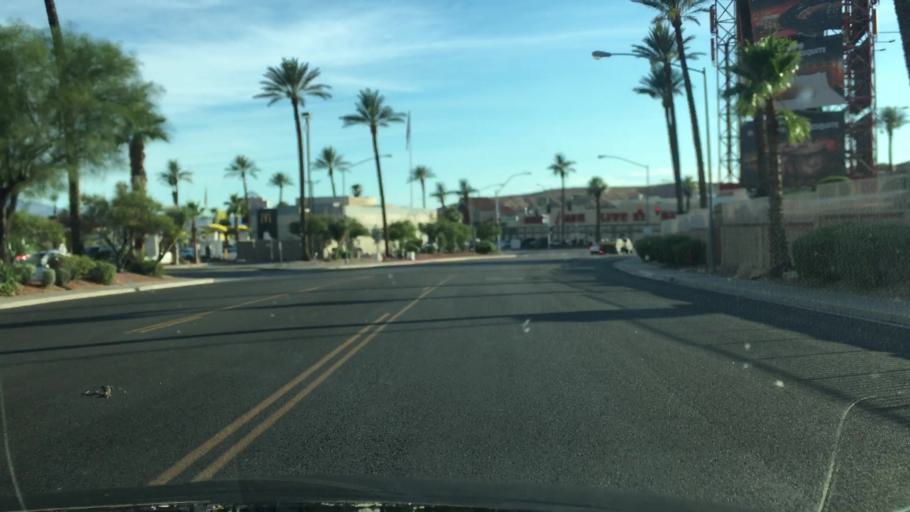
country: US
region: Nevada
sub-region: Clark County
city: Mesquite
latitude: 36.8159
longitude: -114.0639
